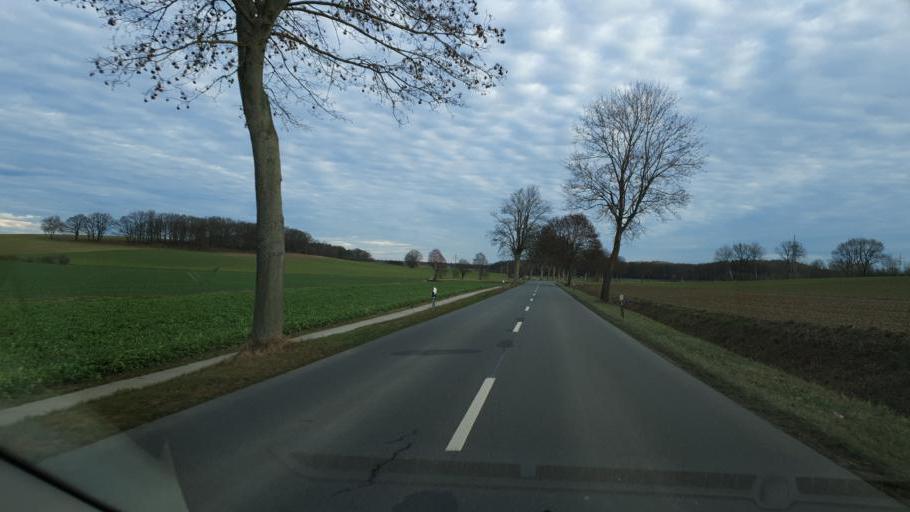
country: DE
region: Lower Saxony
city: Barum
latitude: 53.0560
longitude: 10.5227
